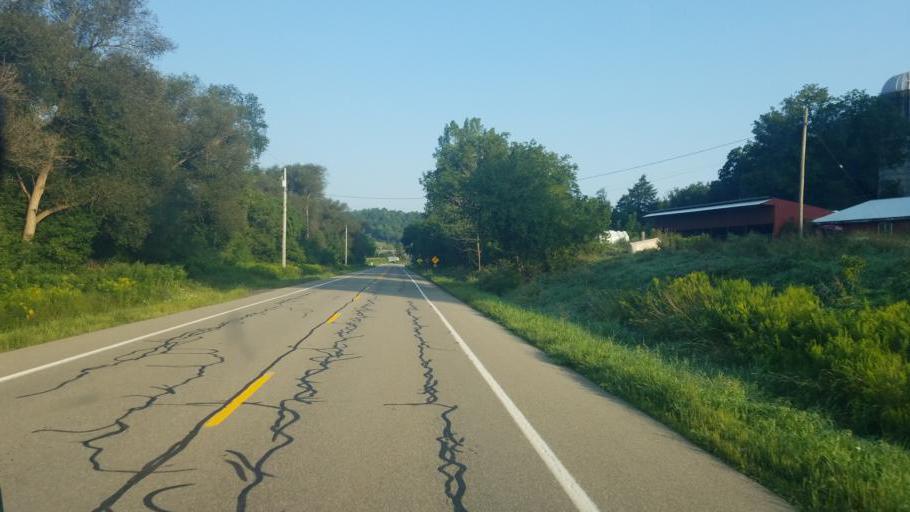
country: US
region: Pennsylvania
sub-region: Tioga County
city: Westfield
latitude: 42.0242
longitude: -77.5312
